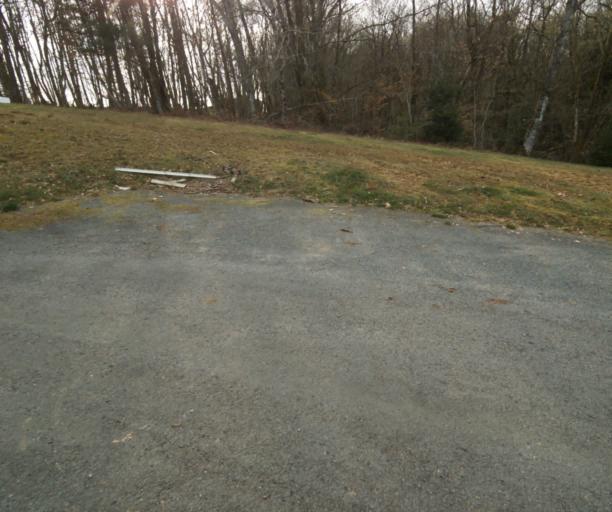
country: FR
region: Limousin
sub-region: Departement de la Correze
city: Naves
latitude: 45.3123
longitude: 1.7551
